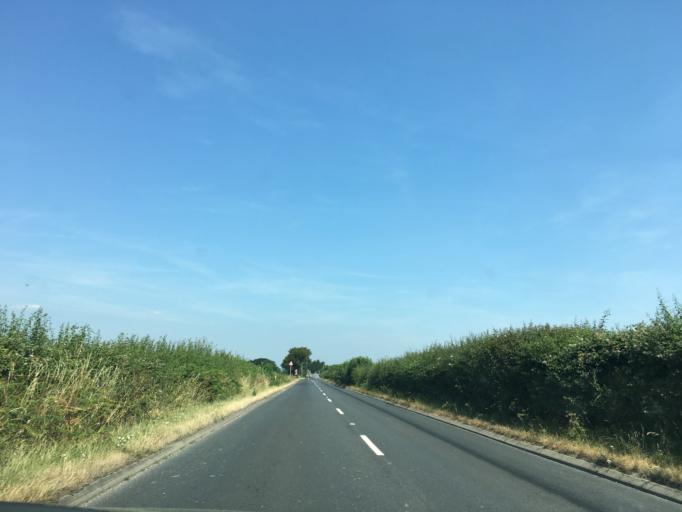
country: GB
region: England
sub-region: Isle of Wight
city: Newport
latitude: 50.7058
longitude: -1.2440
